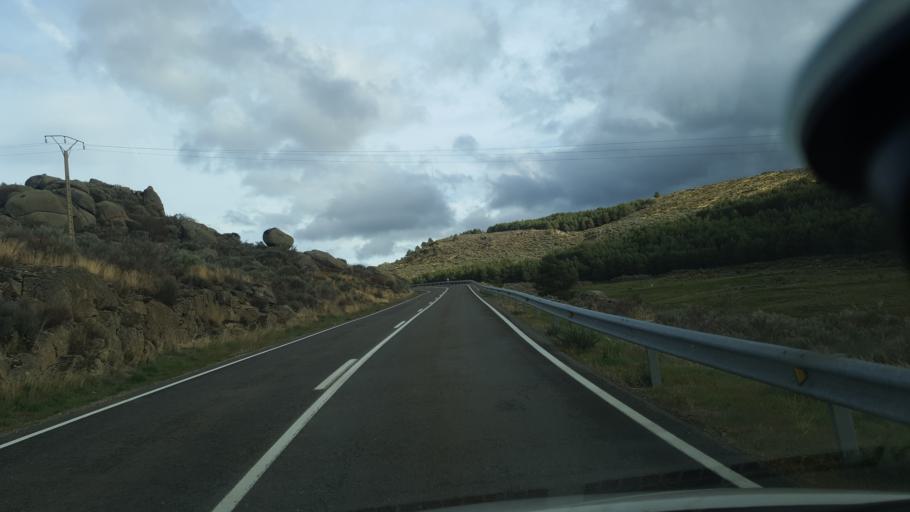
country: ES
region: Castille and Leon
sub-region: Provincia de Avila
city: Hoyocasero
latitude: 40.3898
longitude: -5.0069
